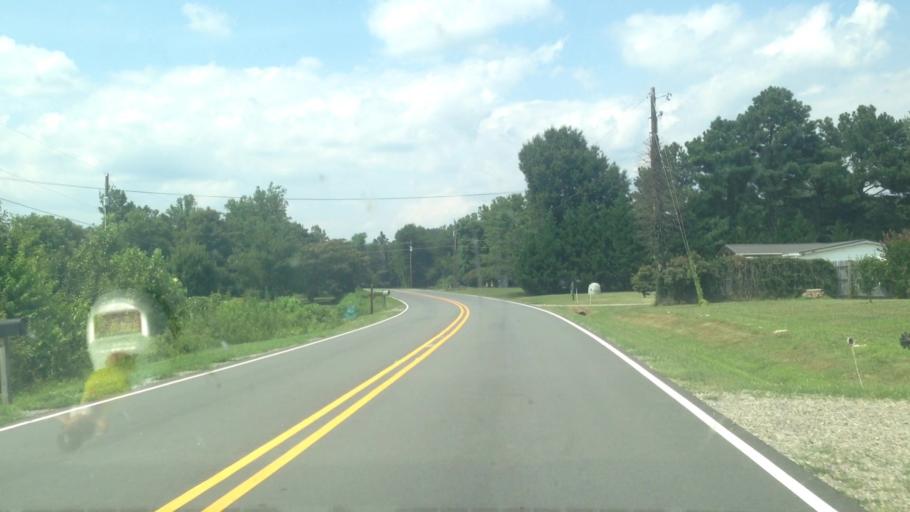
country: US
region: North Carolina
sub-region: Stokes County
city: Danbury
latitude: 36.4059
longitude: -80.0925
